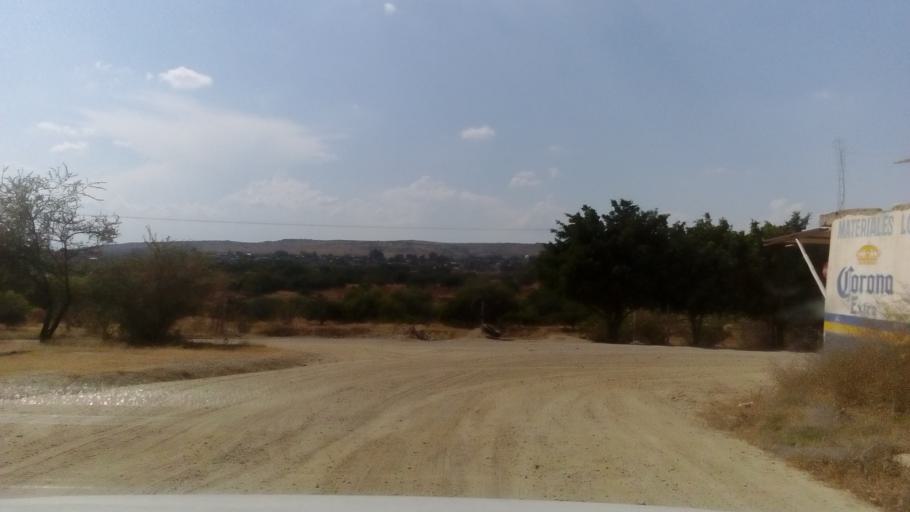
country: MX
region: Guanajuato
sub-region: Silao de la Victoria
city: Loma de Yerbabuena
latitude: 21.0683
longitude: -101.4597
